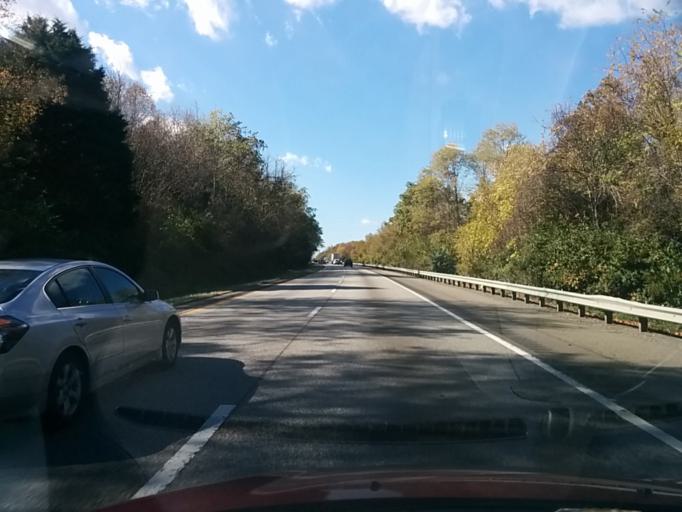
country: US
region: Virginia
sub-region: Botetourt County
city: Fincastle
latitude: 37.4572
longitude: -79.8400
